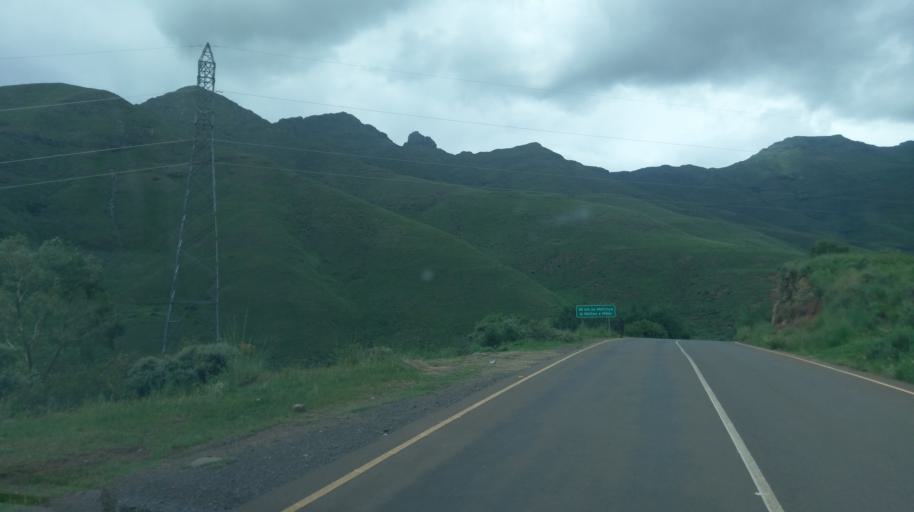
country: LS
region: Butha-Buthe
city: Butha-Buthe
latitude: -29.0503
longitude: 28.3400
